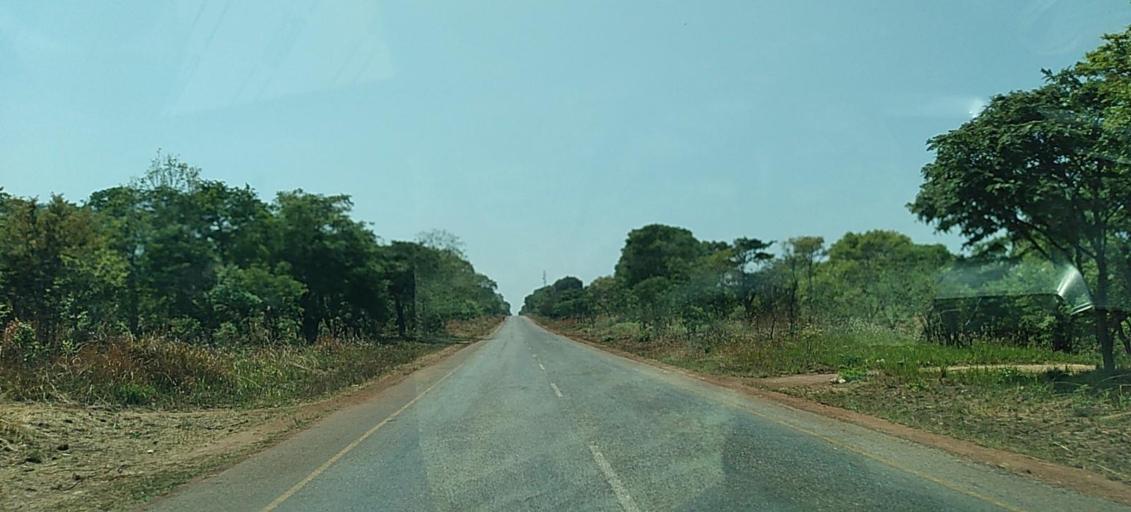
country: ZM
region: North-Western
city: Solwezi
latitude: -12.3638
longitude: 25.9753
